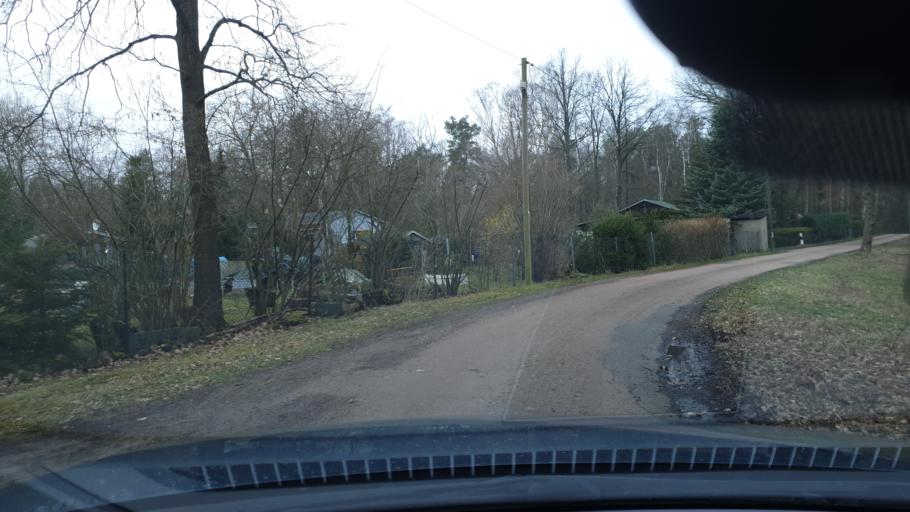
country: DE
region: Saxony-Anhalt
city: Radis
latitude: 51.7473
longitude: 12.5563
